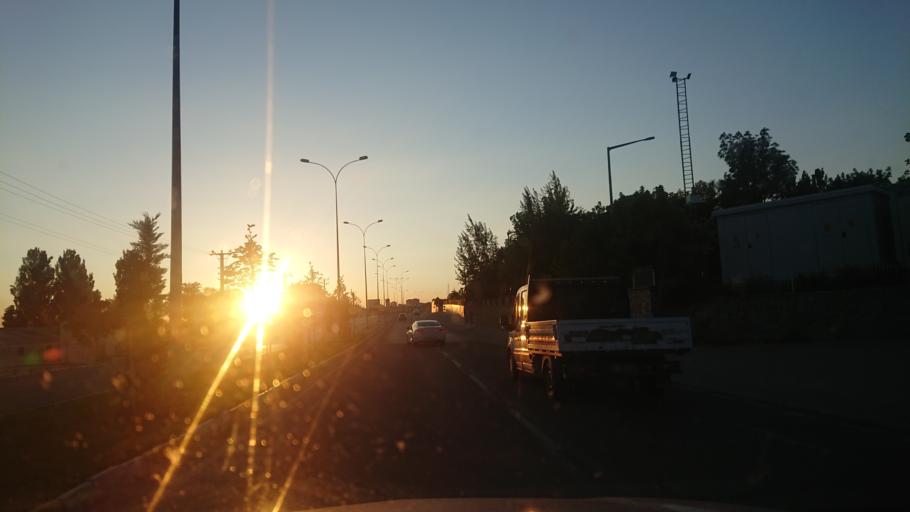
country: TR
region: Aksaray
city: Aksaray
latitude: 38.4017
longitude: 34.0169
